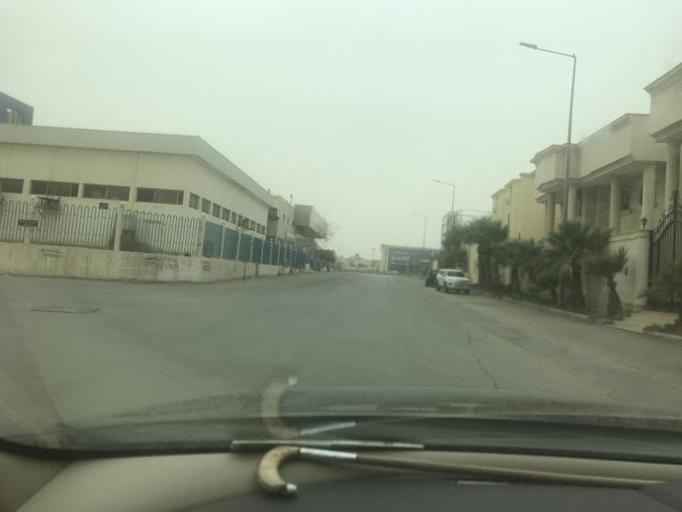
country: SA
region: Ar Riyad
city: Riyadh
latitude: 24.7280
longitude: 46.7866
